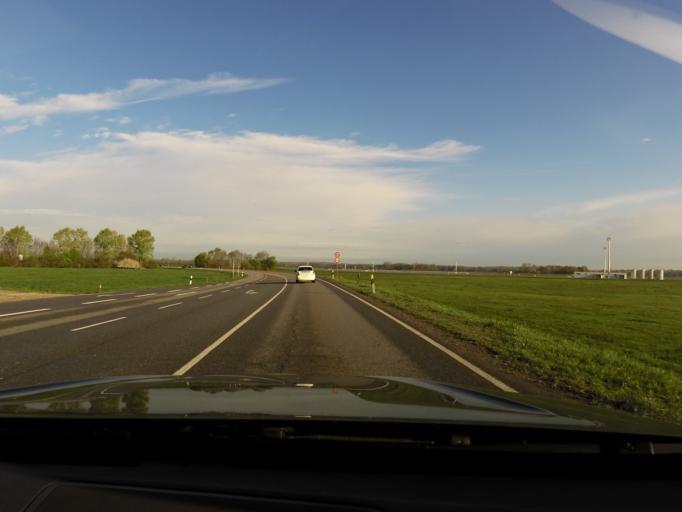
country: DE
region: Bavaria
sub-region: Upper Bavaria
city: Oberding
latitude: 48.3598
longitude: 11.8249
